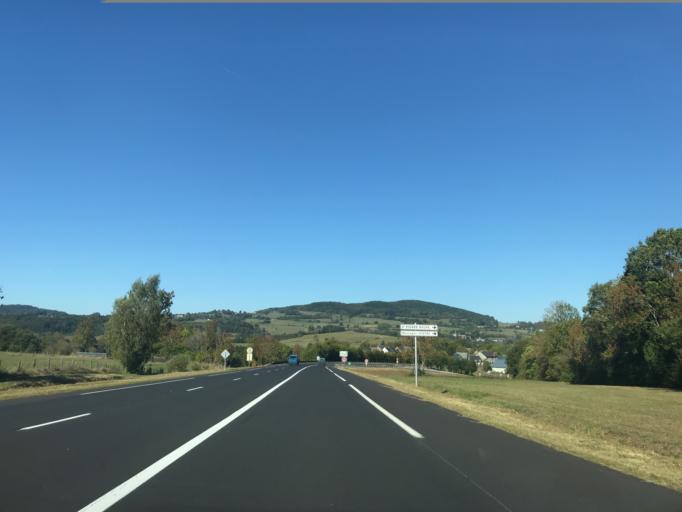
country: FR
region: Auvergne
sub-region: Departement du Puy-de-Dome
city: Gelles
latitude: 45.7207
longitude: 2.8034
